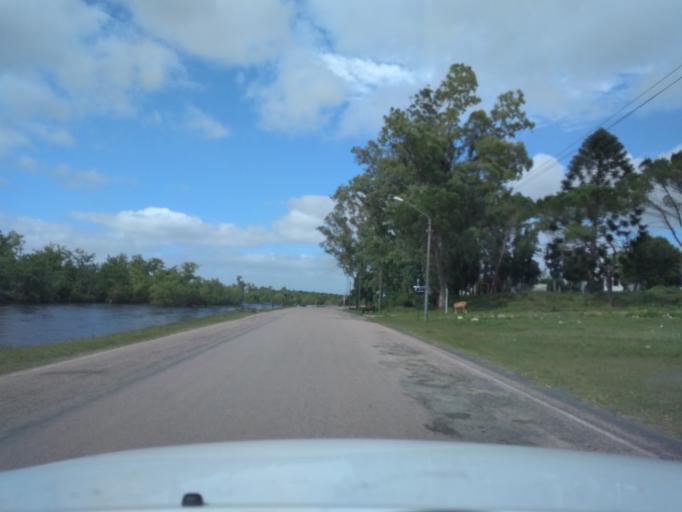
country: UY
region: Florida
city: Florida
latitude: -34.1062
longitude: -56.2048
